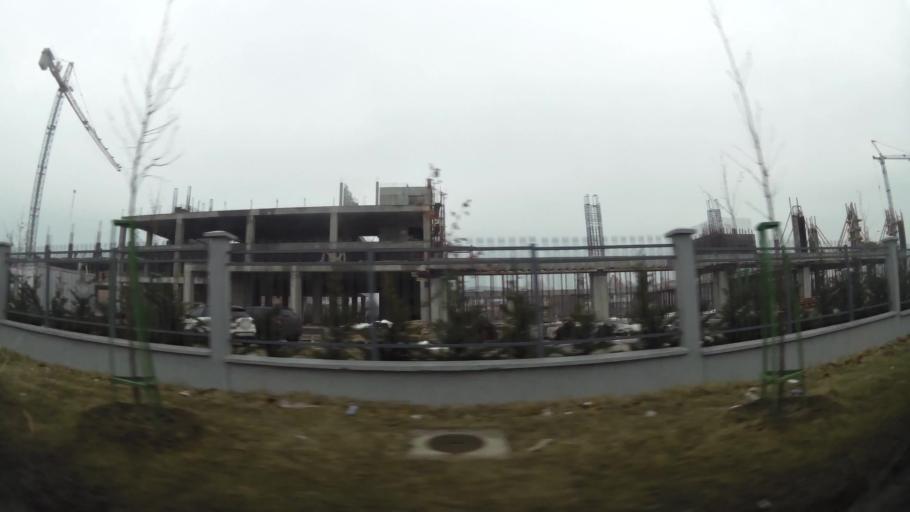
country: MK
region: Suto Orizari
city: Suto Orizare
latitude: 42.0452
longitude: 21.3881
